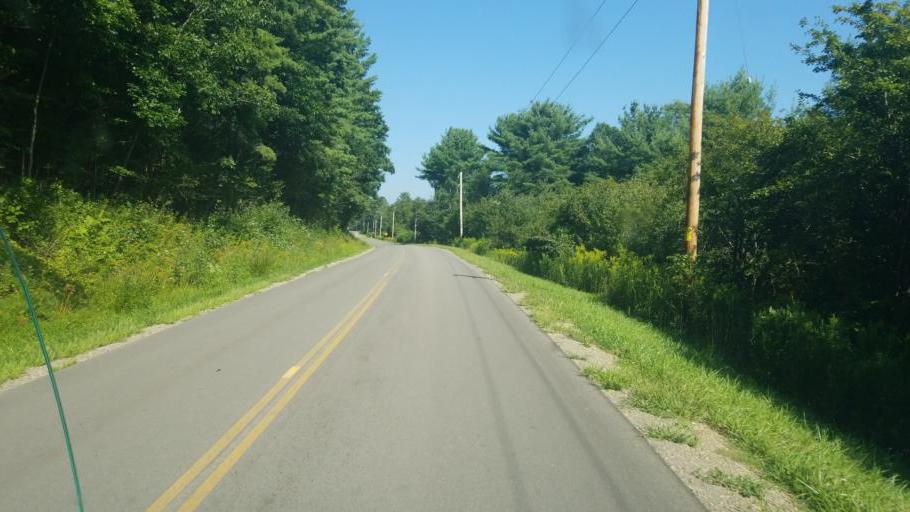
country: US
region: New York
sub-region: Allegany County
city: Bolivar
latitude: 42.0098
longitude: -78.0401
